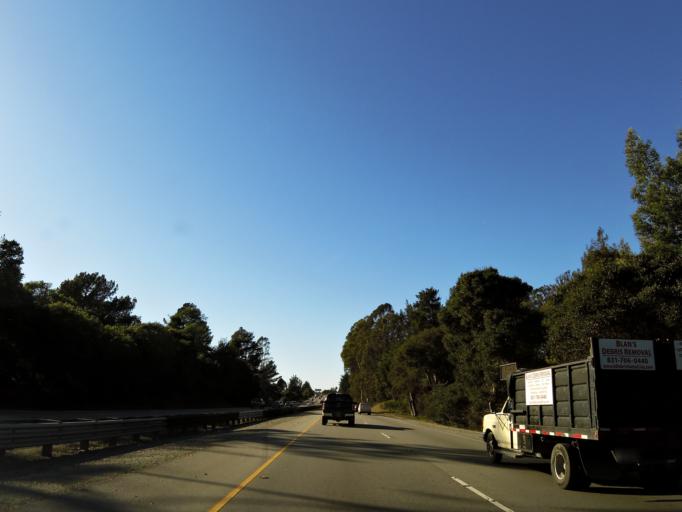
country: US
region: California
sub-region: Santa Cruz County
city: Capitola
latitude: 36.9841
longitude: -121.9424
